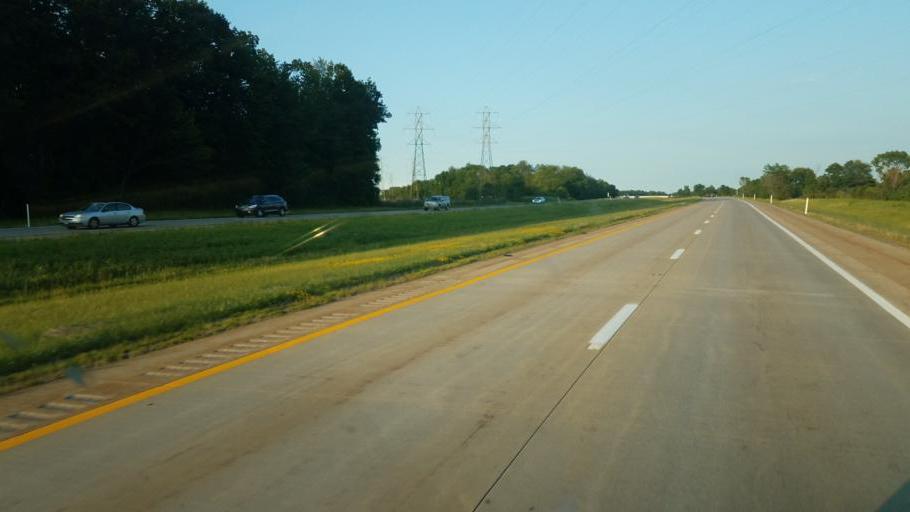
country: US
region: Ohio
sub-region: Ashtabula County
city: Geneva
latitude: 41.7713
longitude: -80.8957
